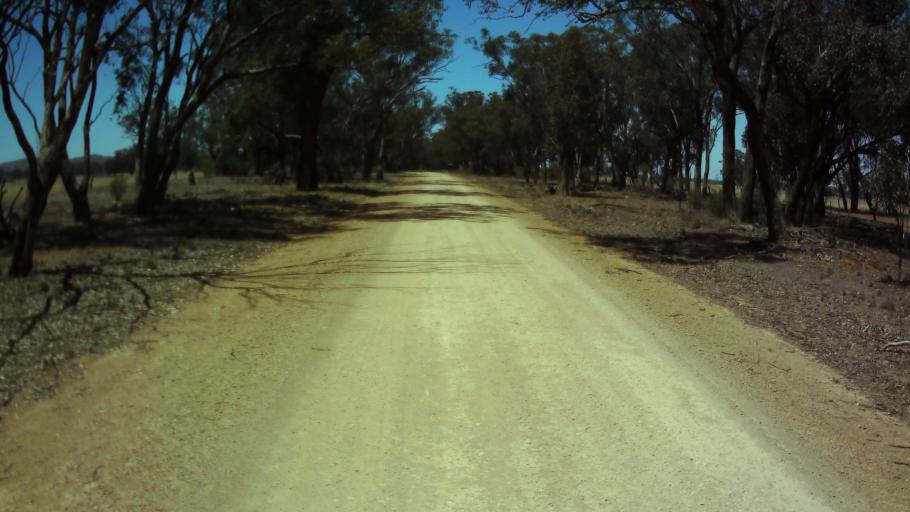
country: AU
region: New South Wales
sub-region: Weddin
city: Grenfell
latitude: -34.0401
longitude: 148.0128
